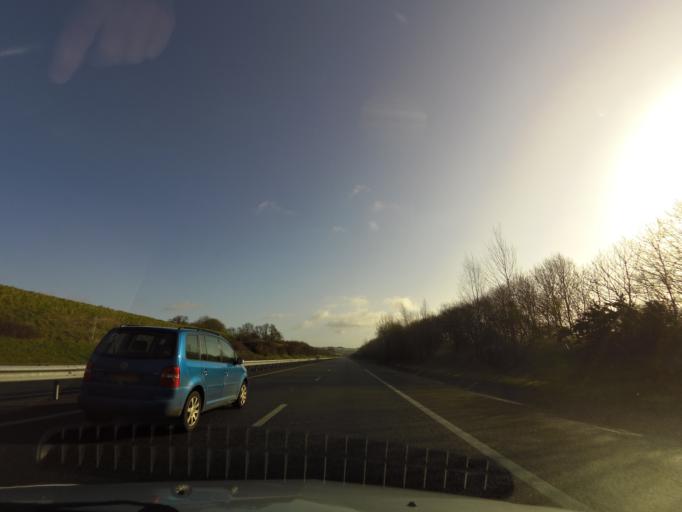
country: FR
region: Brittany
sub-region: Departement d'Ille-et-Vilaine
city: Saint-Jean-sur-Couesnon
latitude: 48.2870
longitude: -1.3837
